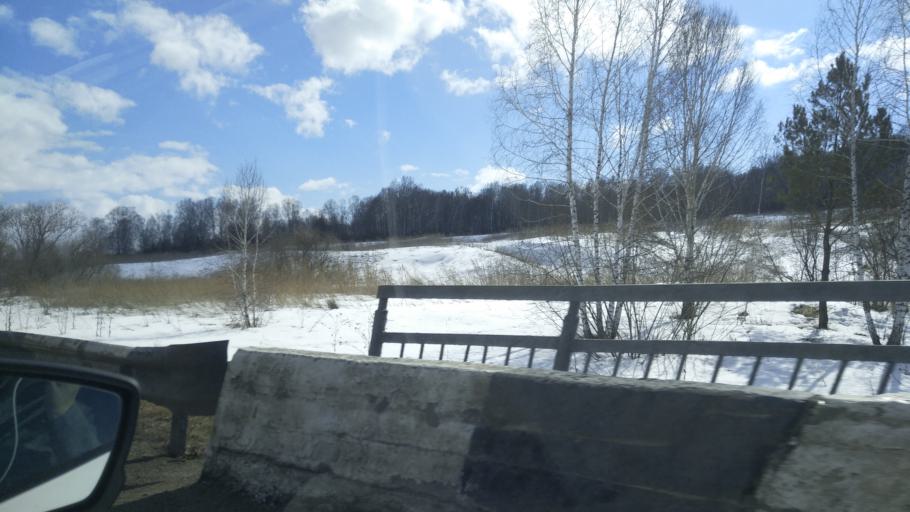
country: RU
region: Kemerovo
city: Yurga
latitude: 55.6731
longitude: 85.1535
